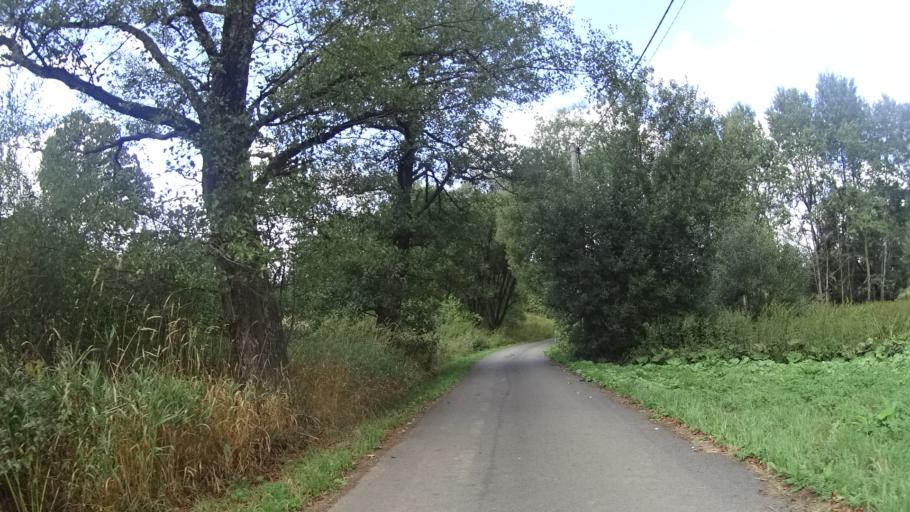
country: CZ
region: Pardubicky
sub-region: Okres Usti nad Orlici
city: Lanskroun
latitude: 49.9202
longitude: 16.5612
